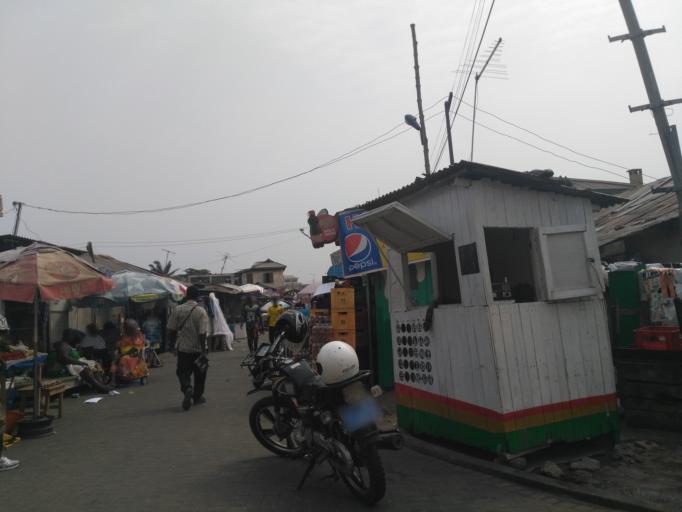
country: GH
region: Greater Accra
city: Accra
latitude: 5.5385
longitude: -0.2153
